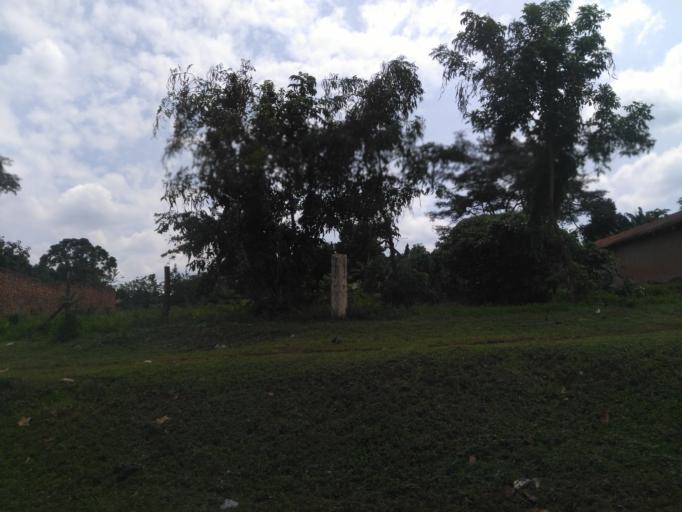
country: UG
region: Central Region
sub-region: Wakiso District
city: Kireka
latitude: 0.4614
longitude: 32.6058
